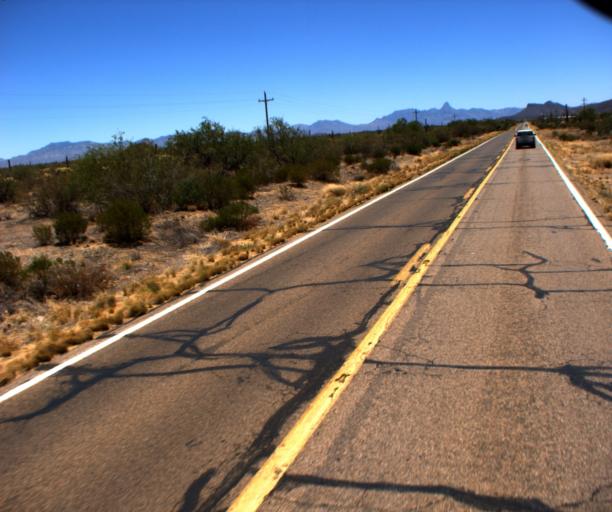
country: US
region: Arizona
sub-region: Pima County
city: Sells
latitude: 31.9438
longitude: -111.9268
